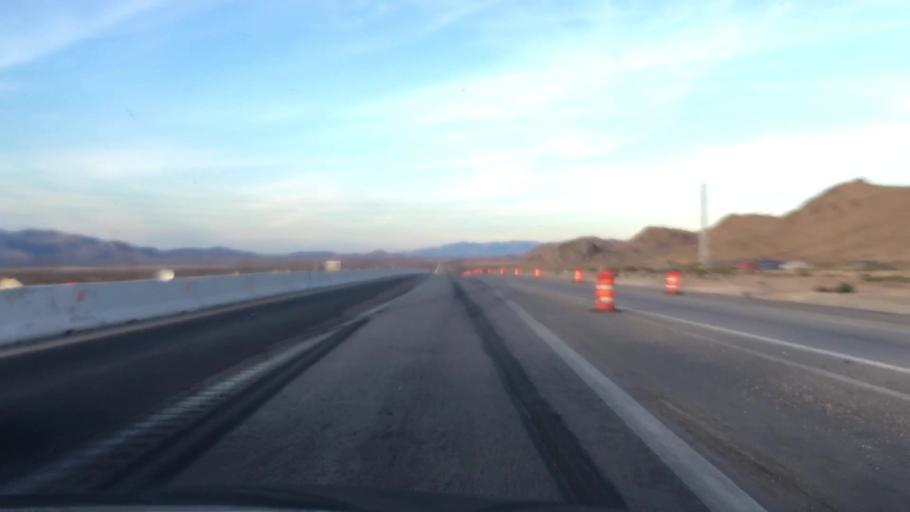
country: US
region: Nevada
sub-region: Clark County
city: Nellis Air Force Base
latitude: 36.3835
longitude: -114.8898
